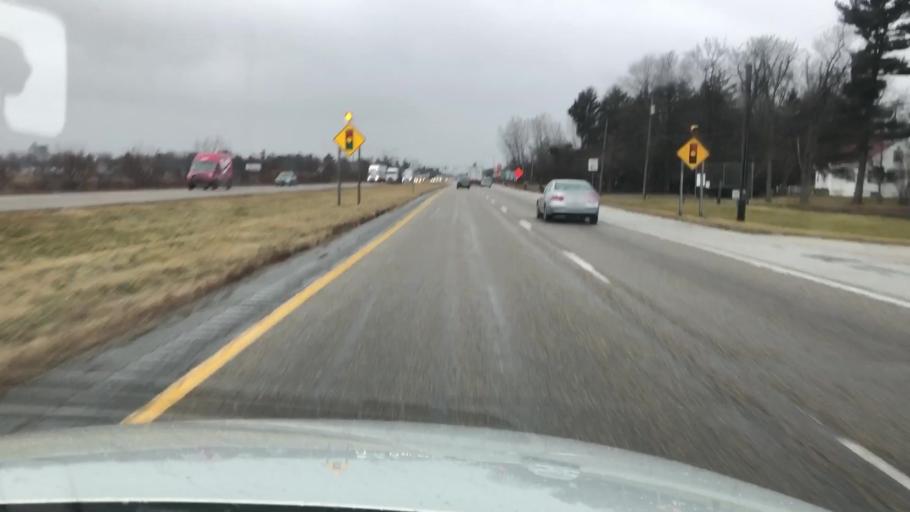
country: US
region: Indiana
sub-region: LaPorte County
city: Wanatah
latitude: 41.4341
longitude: -86.8869
